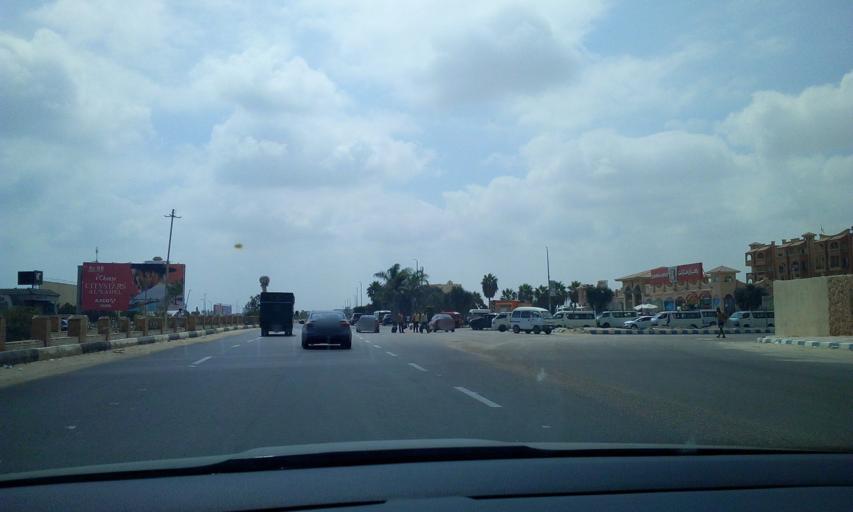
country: EG
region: Muhafazat Matruh
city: Al `Alamayn
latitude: 30.8356
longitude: 28.9590
